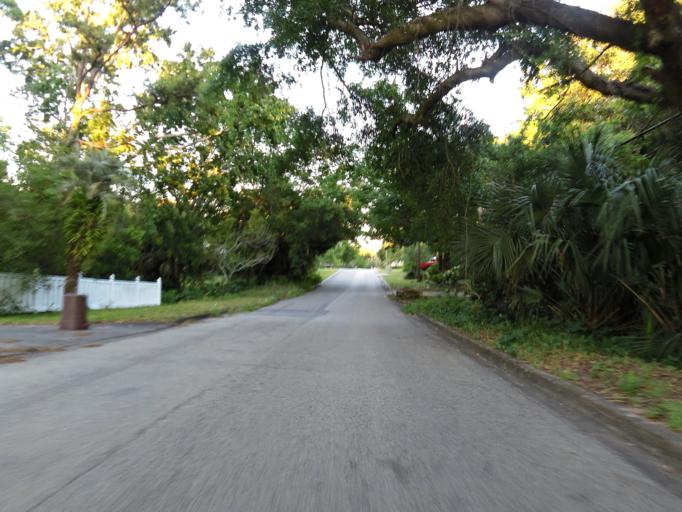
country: US
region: Florida
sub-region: Duval County
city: Jacksonville
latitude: 30.2580
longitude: -81.6295
